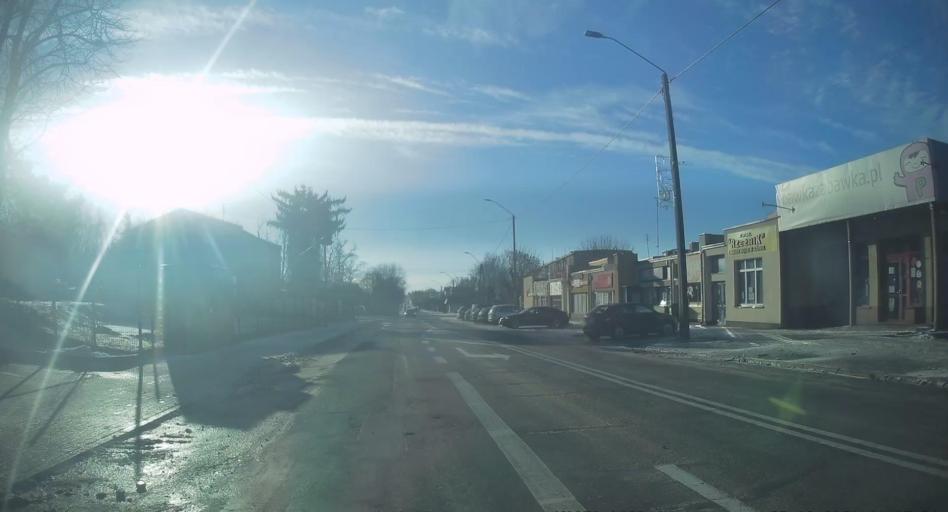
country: PL
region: Lodz Voivodeship
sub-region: Powiat rawski
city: Rawa Mazowiecka
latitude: 51.7596
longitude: 20.2456
